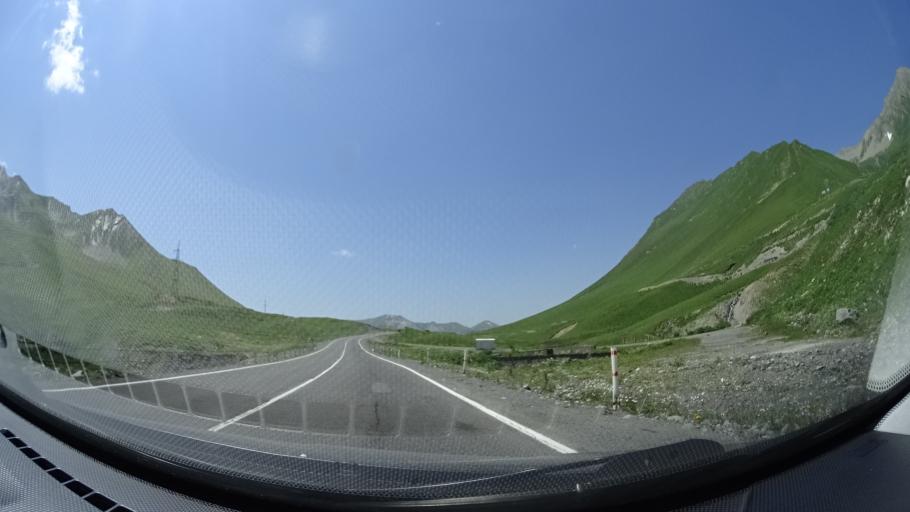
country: GE
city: Gudauri
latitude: 42.5191
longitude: 44.4674
